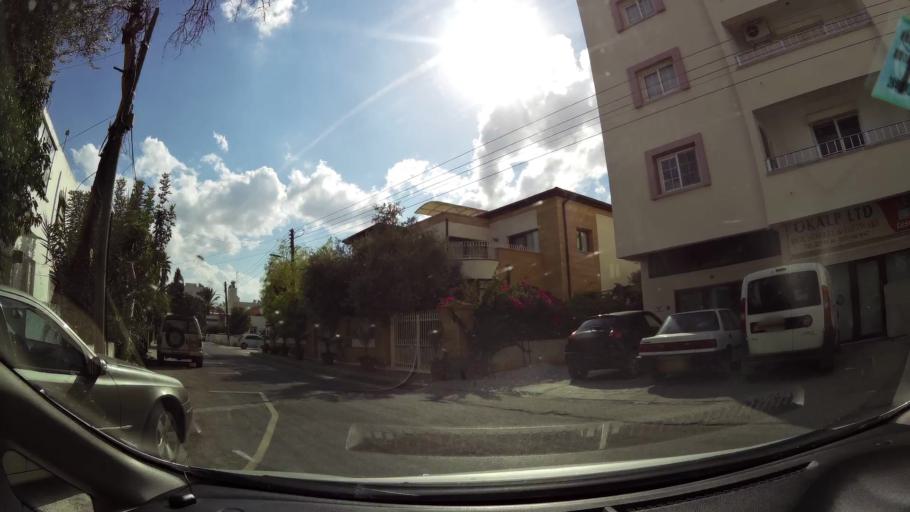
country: CY
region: Lefkosia
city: Nicosia
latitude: 35.1841
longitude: 33.3529
